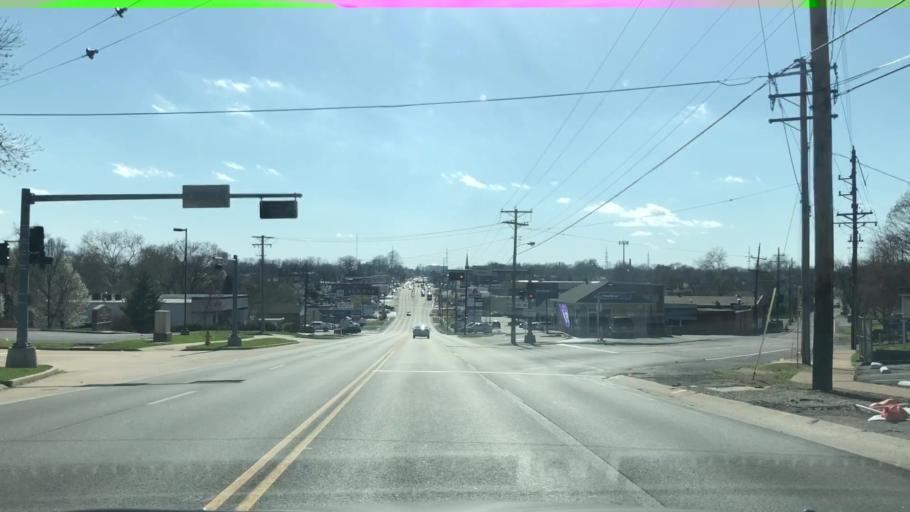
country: US
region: Missouri
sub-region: Saint Louis County
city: Affton
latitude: 38.5543
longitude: -90.3175
